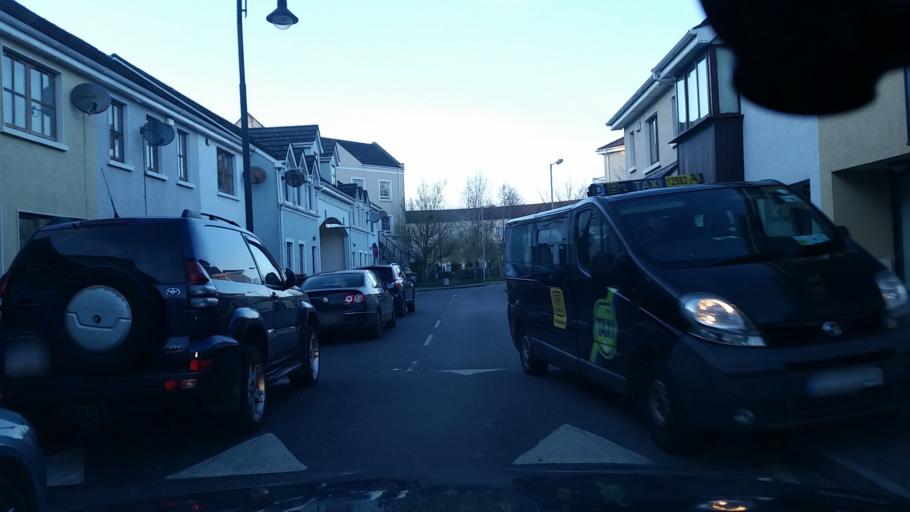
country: IE
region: Leinster
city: Hartstown
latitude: 53.3961
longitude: -6.4398
